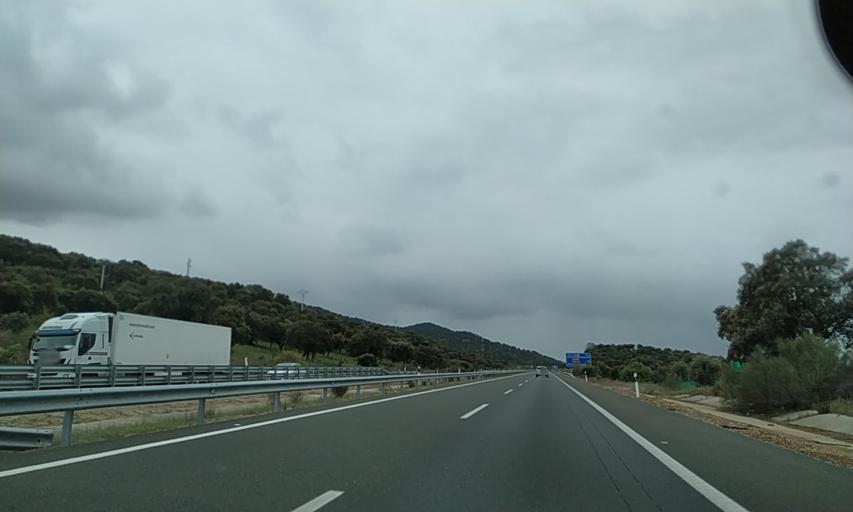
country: ES
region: Extremadura
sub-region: Provincia de Caceres
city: Oliva de Plasencia
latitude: 40.0959
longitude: -6.0687
